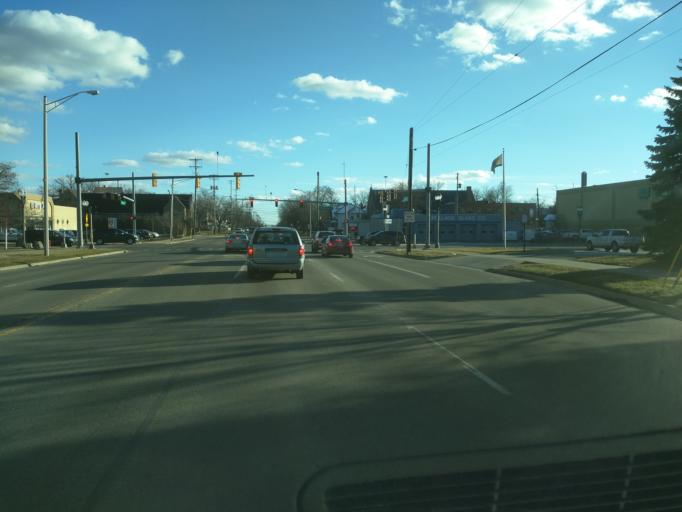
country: US
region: Michigan
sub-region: Ingham County
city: Lansing
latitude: 42.7341
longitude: -84.5379
